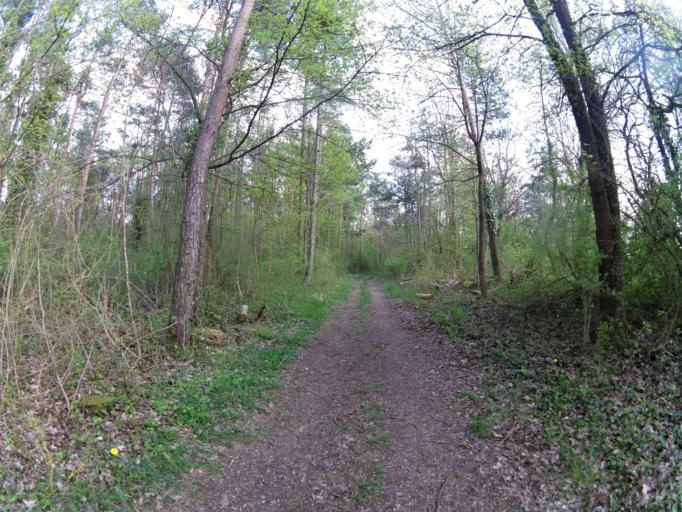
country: DE
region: Bavaria
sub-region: Regierungsbezirk Unterfranken
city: Winterhausen
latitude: 49.6977
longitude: 10.0094
